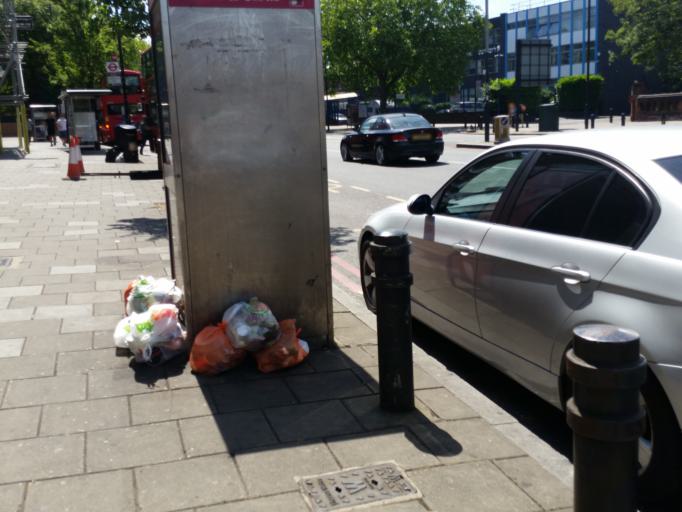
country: GB
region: England
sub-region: Greater London
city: Harringay
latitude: 51.5728
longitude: -0.0725
